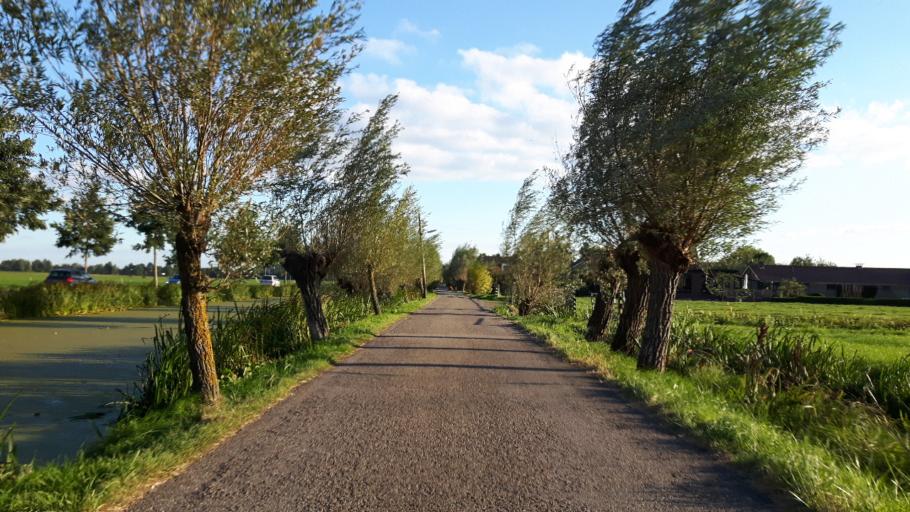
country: NL
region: Utrecht
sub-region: Gemeente Oudewater
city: Oudewater
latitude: 52.0434
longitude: 4.8542
